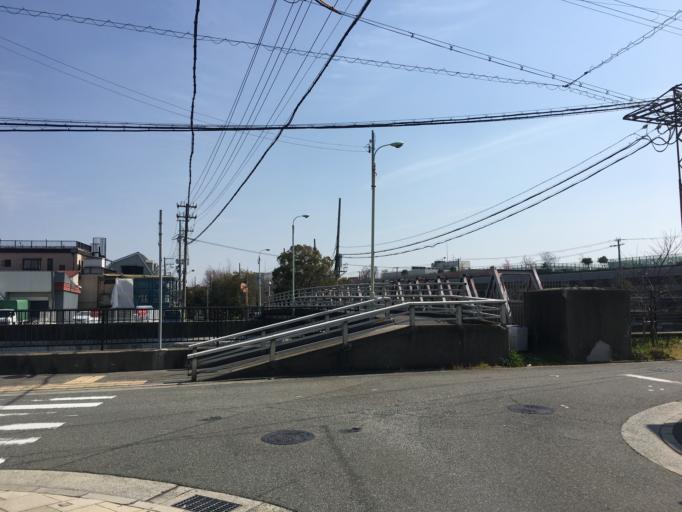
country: JP
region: Hyogo
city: Amagasaki
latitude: 34.7116
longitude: 135.4207
